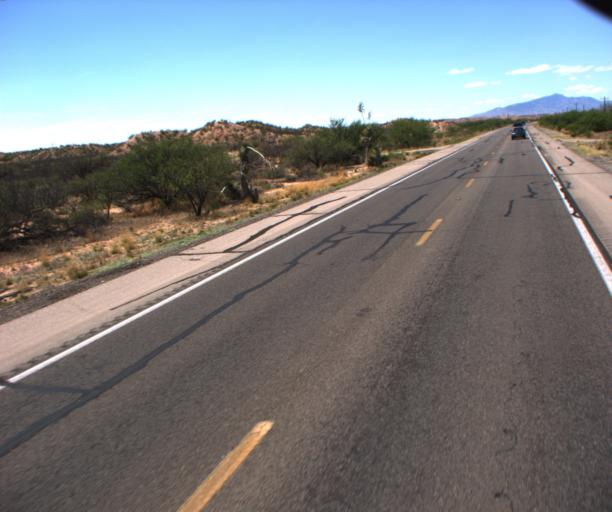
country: US
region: Arizona
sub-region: Cochise County
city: Benson
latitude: 31.9250
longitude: -110.2739
